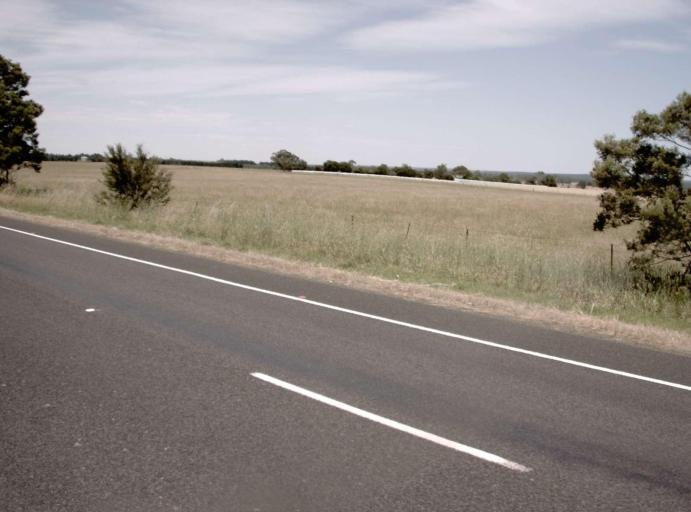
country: AU
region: Victoria
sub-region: Wellington
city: Heyfield
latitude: -38.1176
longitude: 146.8656
